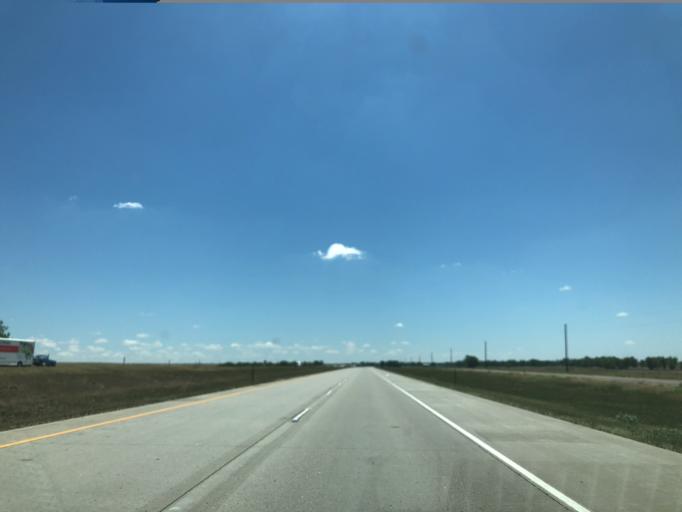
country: US
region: Colorado
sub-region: Arapahoe County
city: Byers
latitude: 39.5198
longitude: -103.9824
